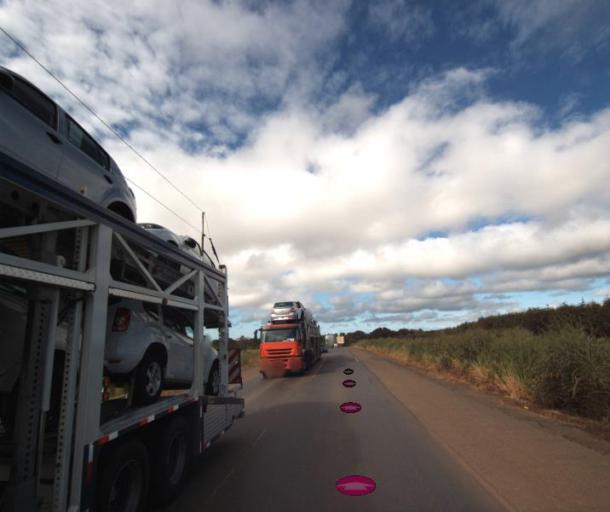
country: BR
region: Goias
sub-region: Uruacu
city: Uruacu
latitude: -14.7523
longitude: -49.2544
